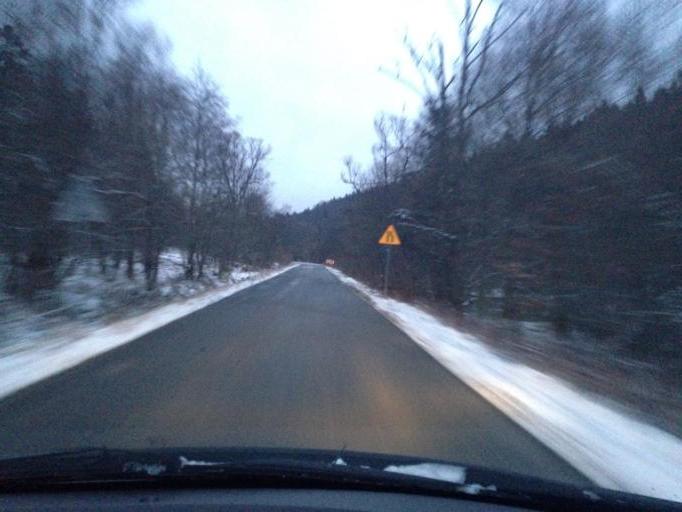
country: PL
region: Subcarpathian Voivodeship
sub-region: Powiat jasielski
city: Krempna
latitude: 49.5082
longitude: 21.5402
